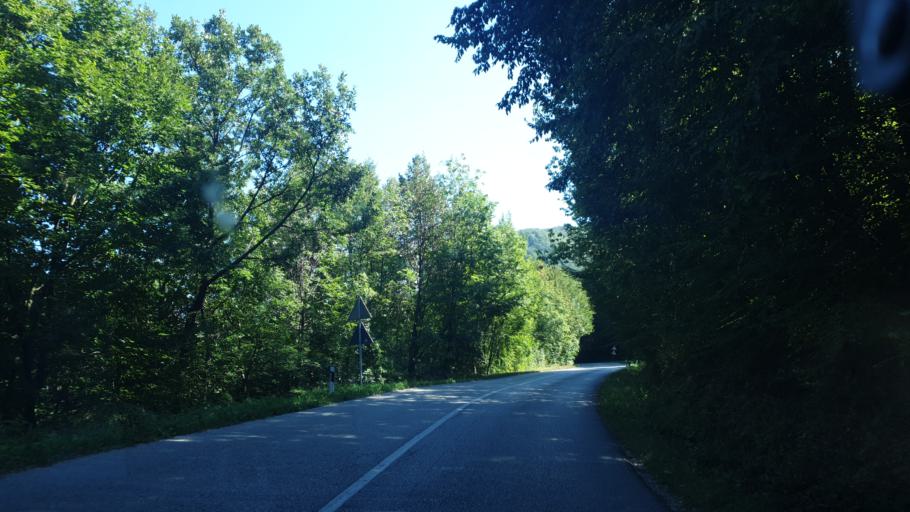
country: RS
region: Central Serbia
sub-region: Kolubarski Okrug
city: Mionica
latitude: 44.1560
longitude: 20.0061
